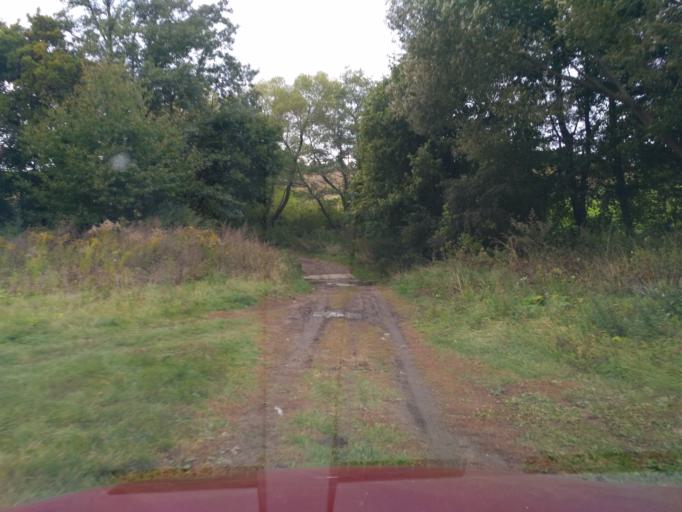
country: SK
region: Presovsky
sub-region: Okres Presov
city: Presov
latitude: 48.8980
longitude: 21.3324
